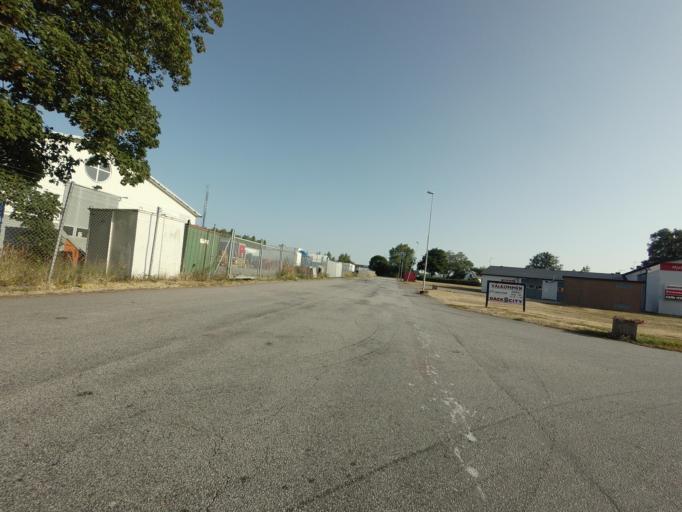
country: SE
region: Skane
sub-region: Landskrona
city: Landskrona
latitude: 55.8713
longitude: 12.8707
